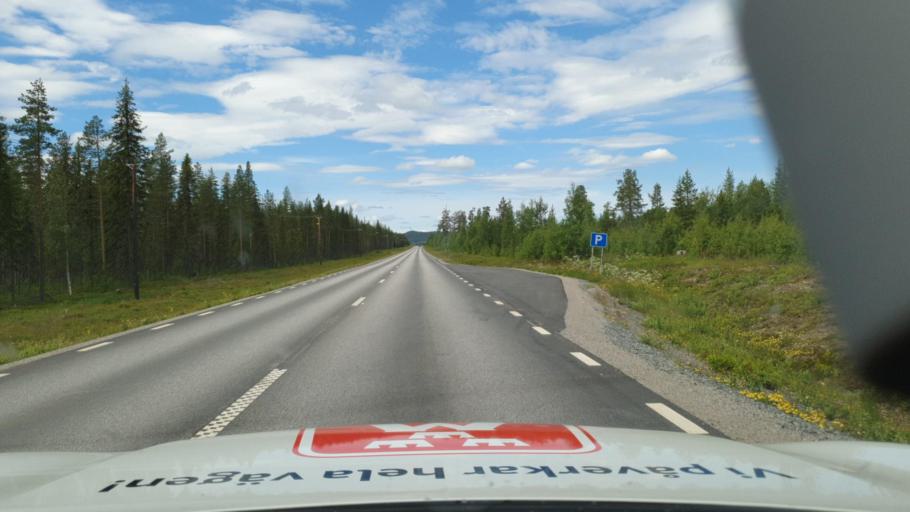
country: SE
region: Vaesterbotten
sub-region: Norsjo Kommun
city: Norsjoe
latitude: 65.2383
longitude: 19.7197
